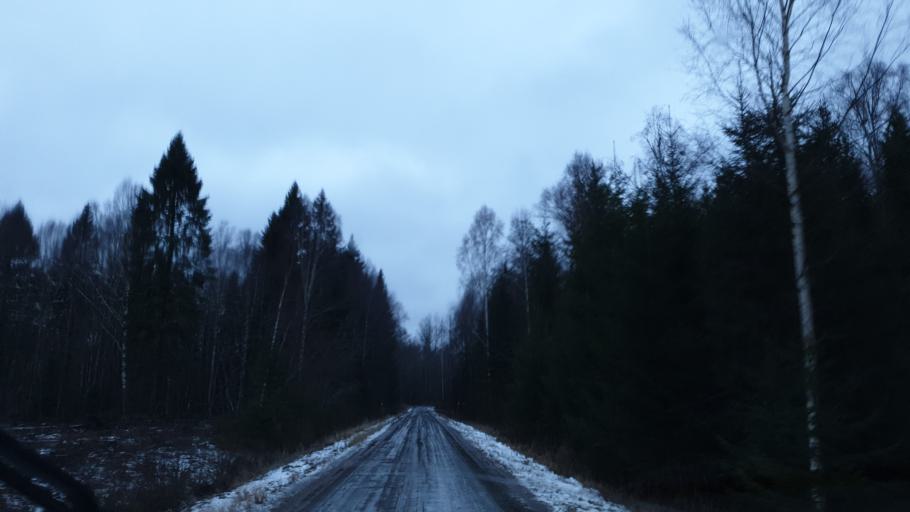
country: SE
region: Uppsala
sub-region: Tierps Kommun
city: Tierp
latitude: 60.3475
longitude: 17.4663
